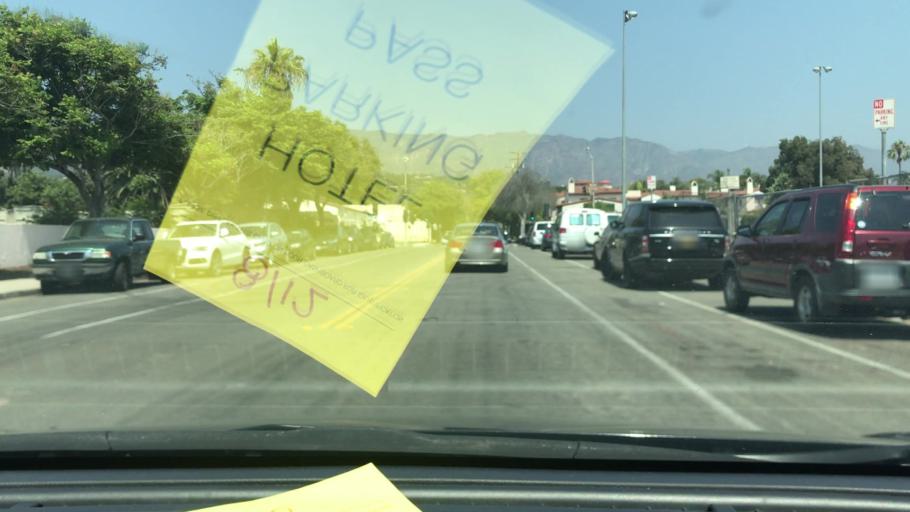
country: US
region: California
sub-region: Santa Barbara County
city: Santa Barbara
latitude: 34.4172
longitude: -119.6746
